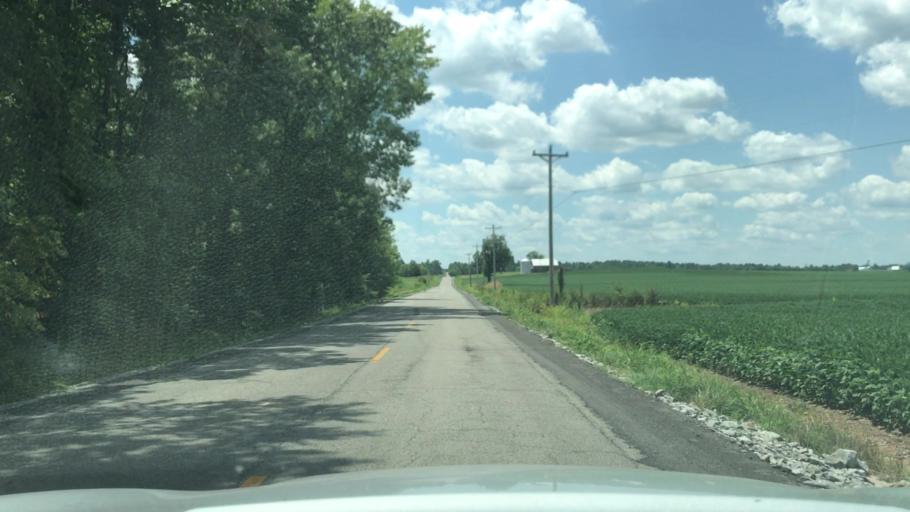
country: US
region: Kentucky
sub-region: Muhlenberg County
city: Greenville
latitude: 37.1323
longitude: -87.2822
